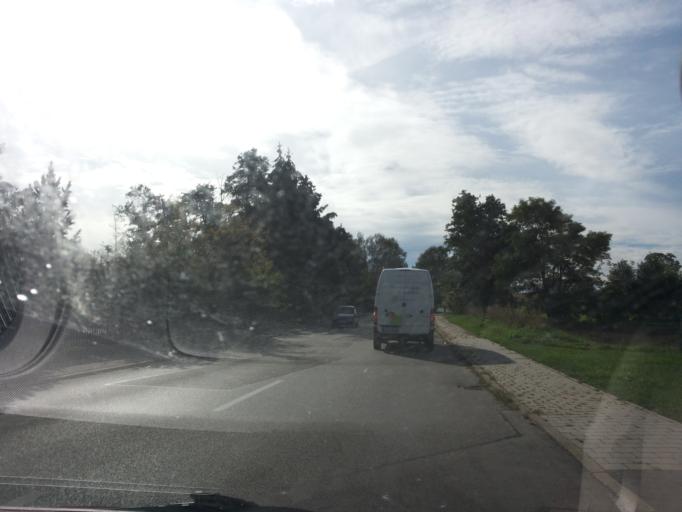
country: DE
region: Bavaria
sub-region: Upper Bavaria
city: Lenting
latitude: 48.8070
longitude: 11.5008
